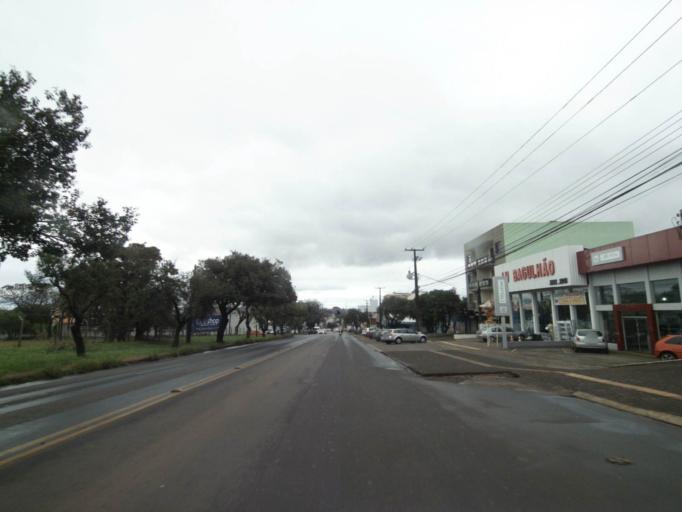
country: BR
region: Parana
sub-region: Foz Do Iguacu
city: Foz do Iguacu
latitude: -25.5170
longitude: -54.5762
